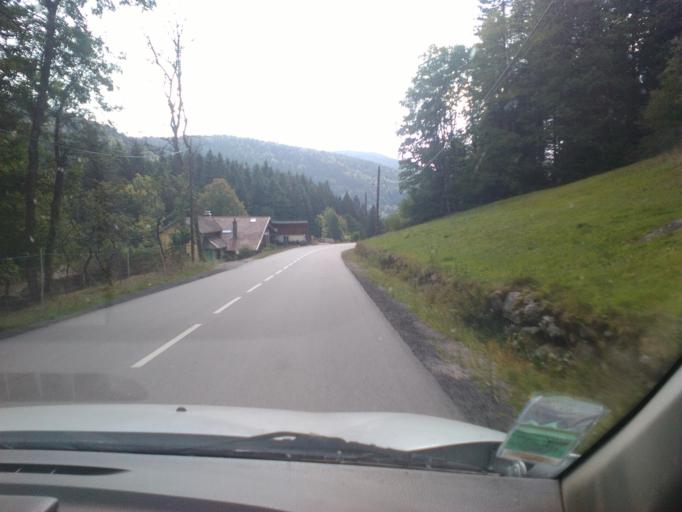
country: FR
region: Lorraine
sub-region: Departement des Vosges
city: Gerardmer
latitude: 48.0396
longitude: 6.8574
